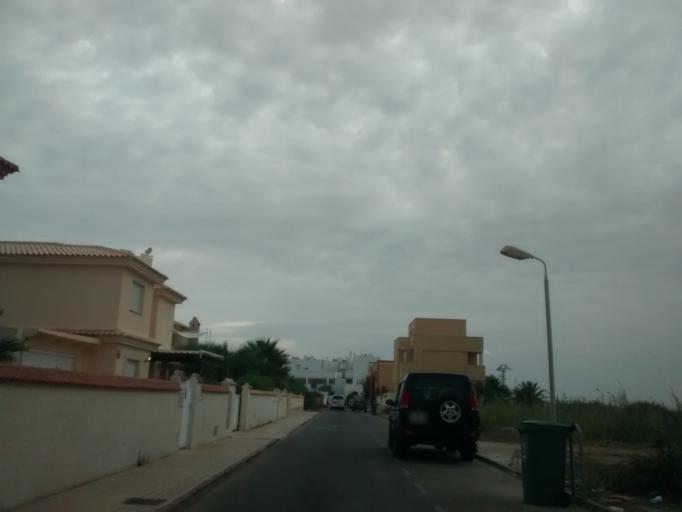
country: ES
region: Murcia
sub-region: Murcia
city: San Pedro del Pinatar
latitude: 37.7795
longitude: -0.7530
